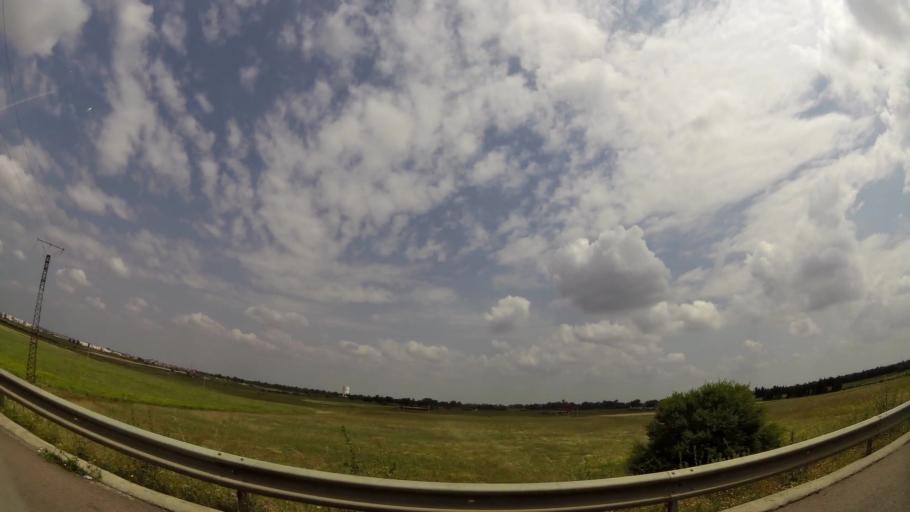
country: MA
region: Rabat-Sale-Zemmour-Zaer
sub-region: Khemisset
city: Tiflet
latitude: 33.9782
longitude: -6.5173
